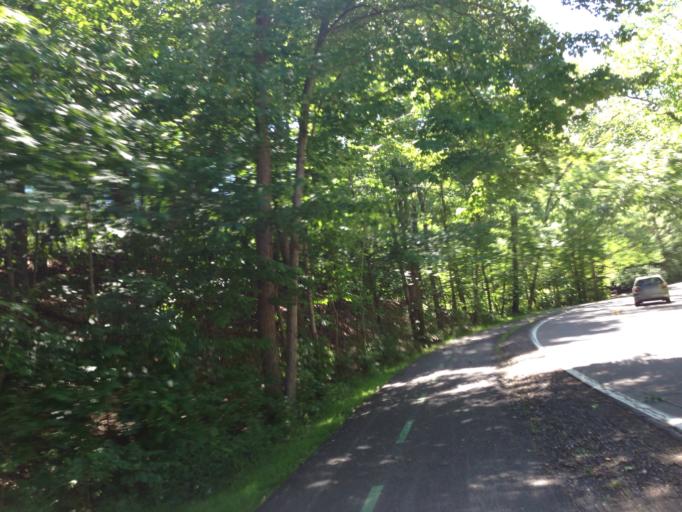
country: US
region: Ohio
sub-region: Cuyahoga County
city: Strongsville
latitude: 41.3411
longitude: -81.8323
